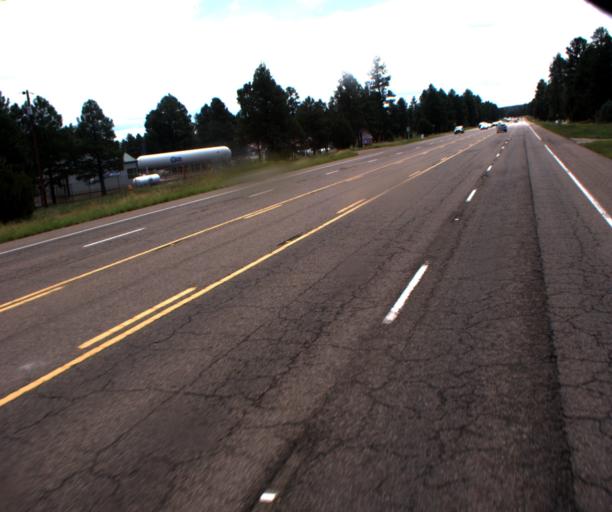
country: US
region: Arizona
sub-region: Navajo County
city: Heber-Overgaard
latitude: 34.4024
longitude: -110.5637
